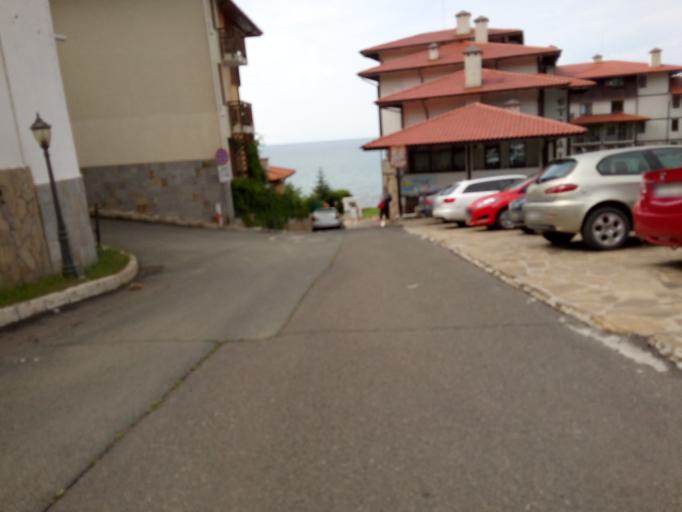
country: BG
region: Burgas
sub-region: Obshtina Nesebur
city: Sveti Vlas
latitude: 42.7065
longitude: 27.7771
